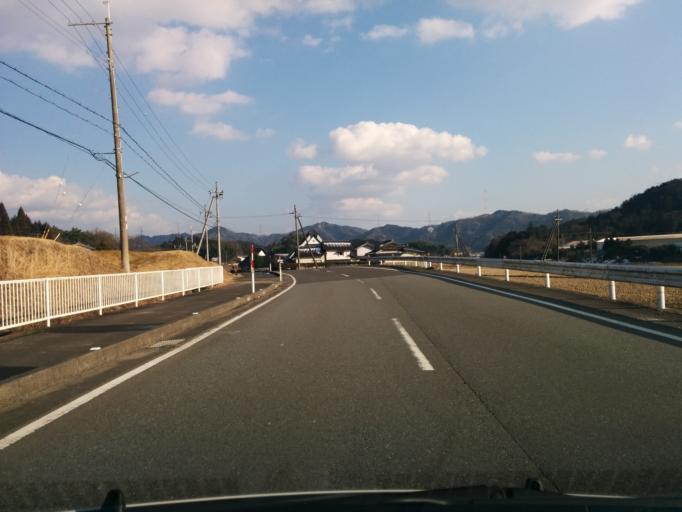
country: JP
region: Kyoto
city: Ayabe
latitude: 35.3624
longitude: 135.2094
